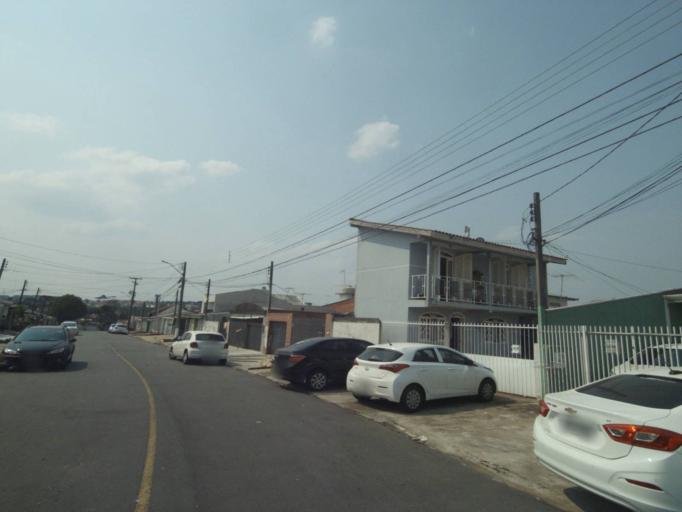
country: BR
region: Parana
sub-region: Sao Jose Dos Pinhais
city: Sao Jose dos Pinhais
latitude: -25.5301
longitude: -49.2444
